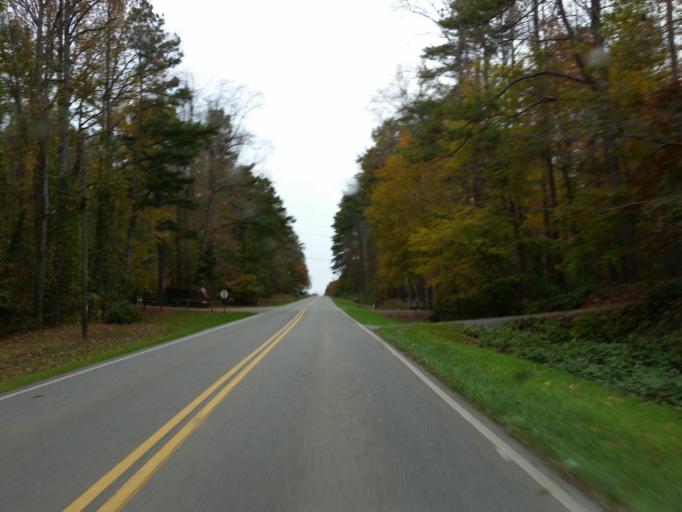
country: US
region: Georgia
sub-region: Pickens County
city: Jasper
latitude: 34.5016
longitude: -84.4356
